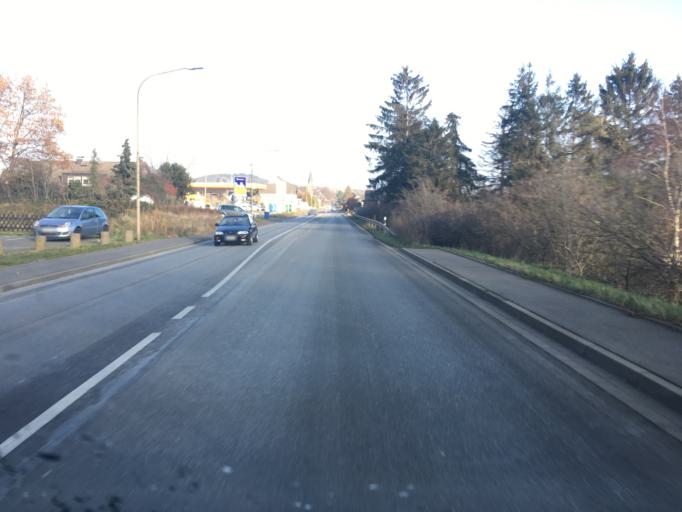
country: DE
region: North Rhine-Westphalia
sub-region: Regierungsbezirk Koln
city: Mechernich
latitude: 50.5882
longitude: 6.6192
